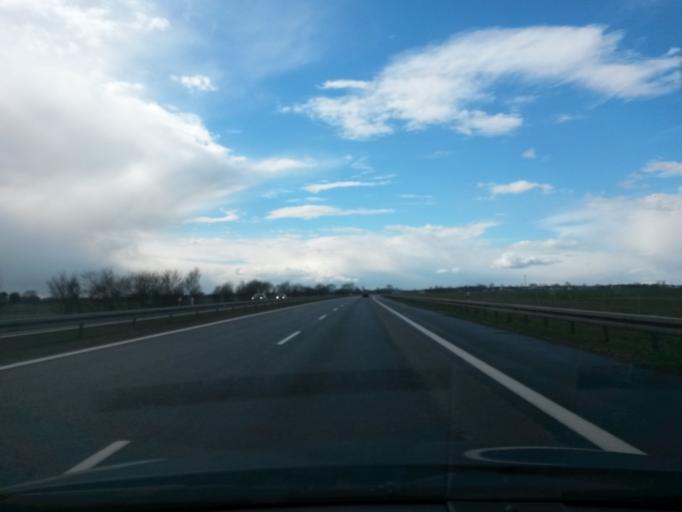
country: PL
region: Greater Poland Voivodeship
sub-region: Powiat slupecki
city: Ladek
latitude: 52.2312
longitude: 17.9087
